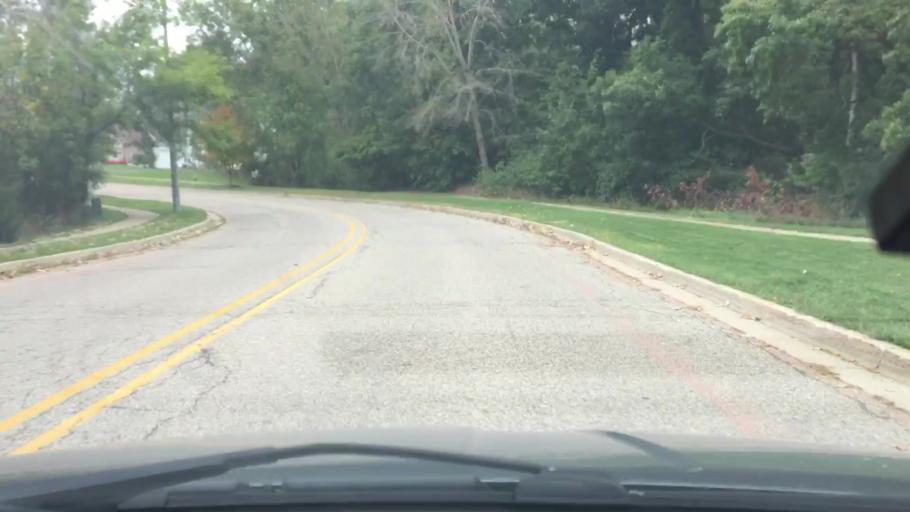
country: US
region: Michigan
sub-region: Livingston County
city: Brighton
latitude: 42.5146
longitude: -83.7816
